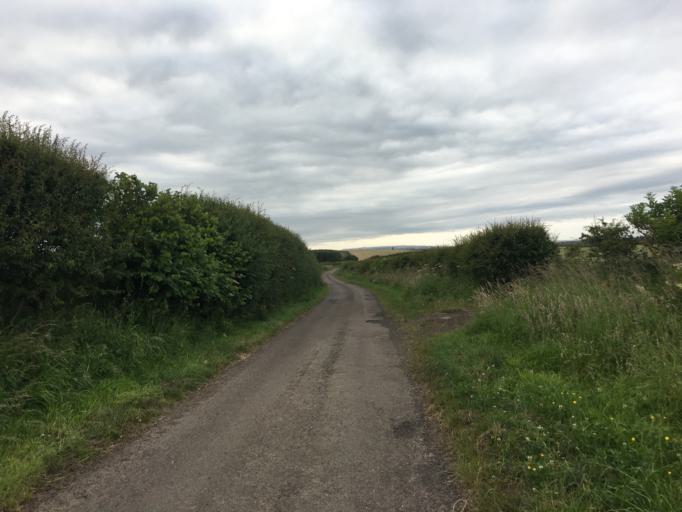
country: GB
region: England
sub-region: Northumberland
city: Lowick
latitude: 55.6569
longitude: -1.9038
